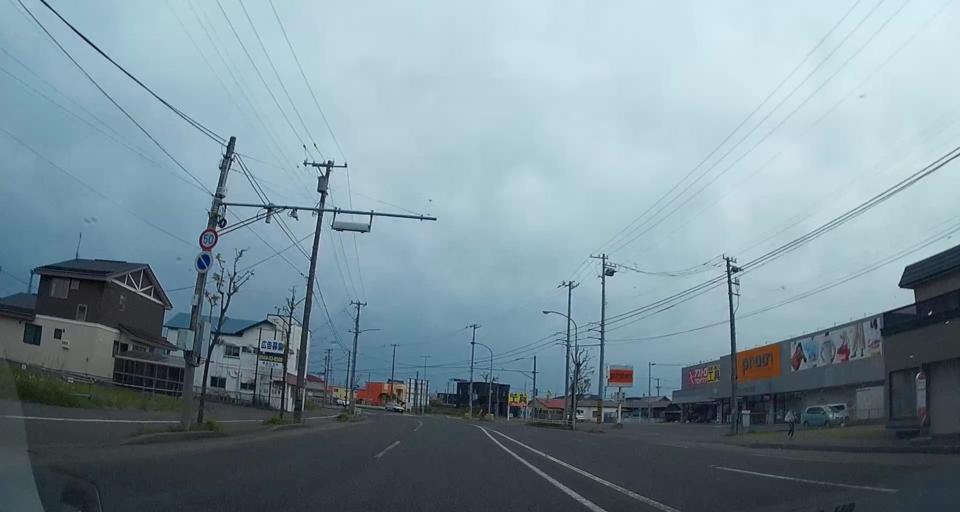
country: JP
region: Hokkaido
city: Tomakomai
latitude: 42.6283
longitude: 141.5935
